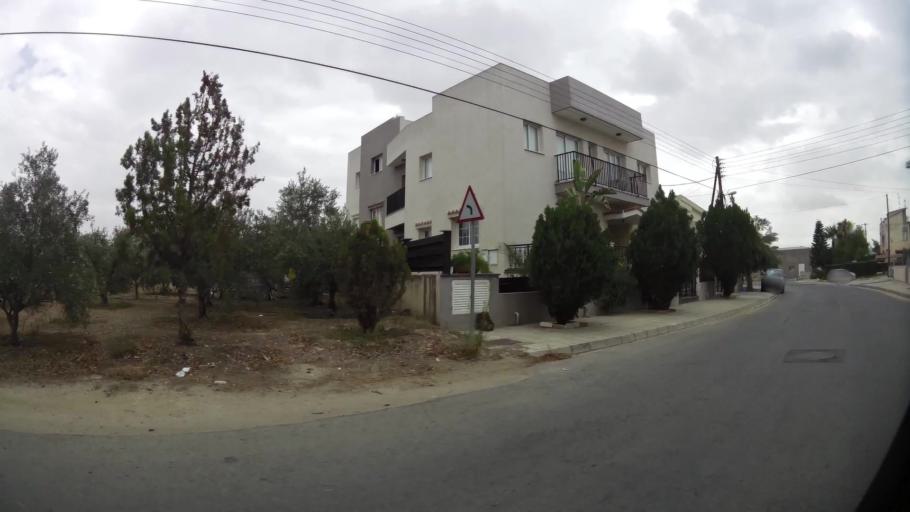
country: CY
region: Lefkosia
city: Geri
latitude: 35.0962
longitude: 33.3772
